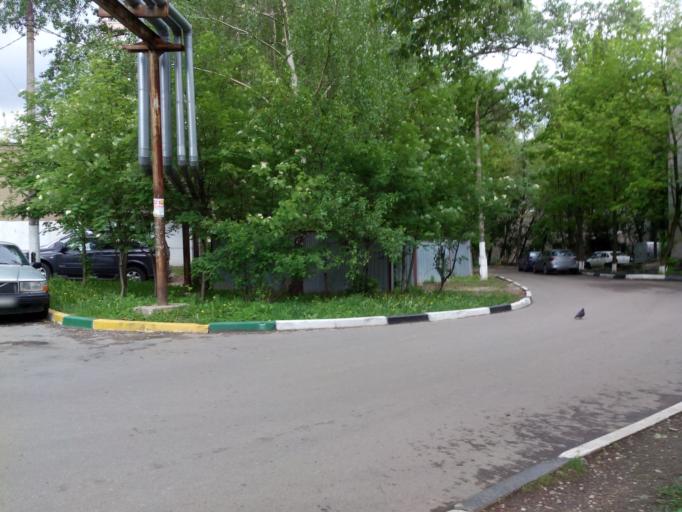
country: RU
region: Moskovskaya
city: Odintsovo
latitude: 55.6695
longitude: 37.2902
